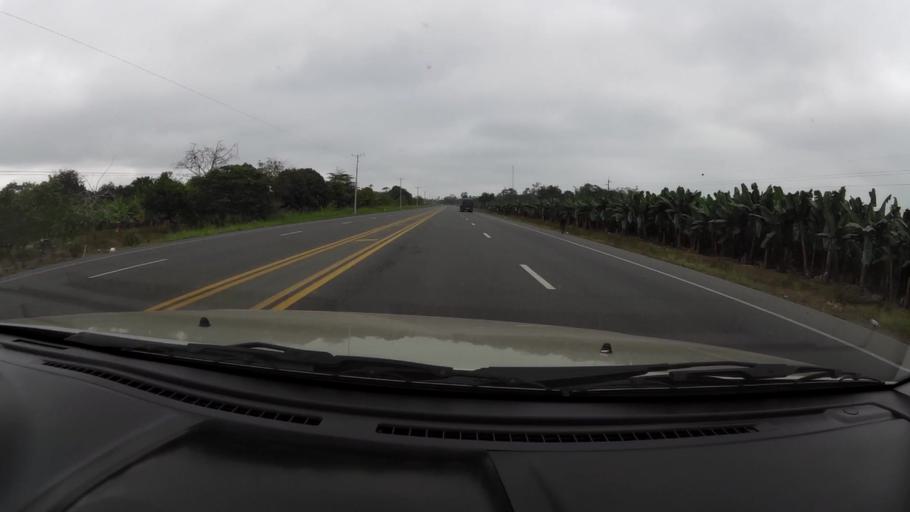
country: EC
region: Guayas
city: Naranjal
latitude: -2.5658
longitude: -79.5679
